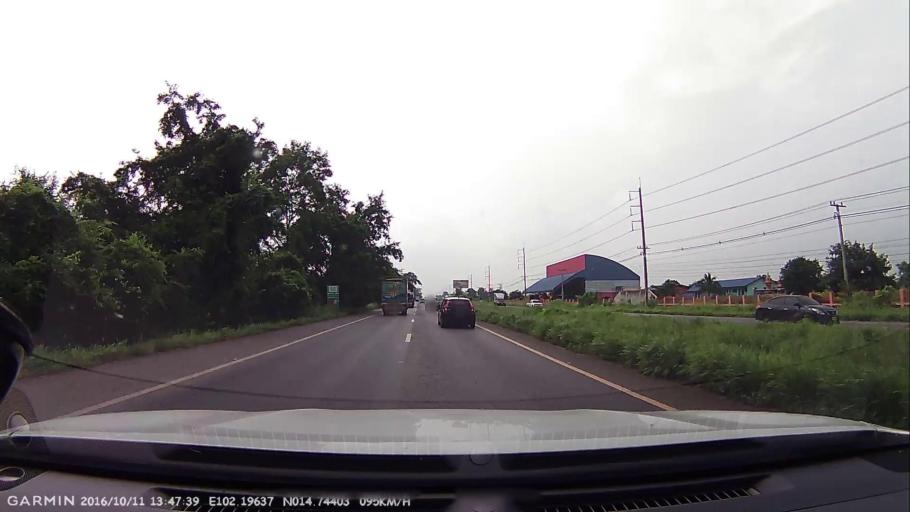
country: TH
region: Nakhon Ratchasima
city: Chok Chai
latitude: 14.7440
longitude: 102.1964
